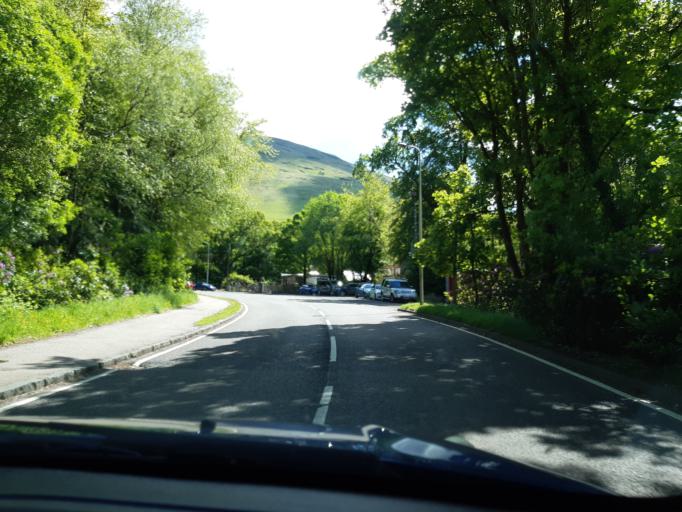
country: GB
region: Scotland
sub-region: Argyll and Bute
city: Garelochhead
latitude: 56.1985
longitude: -4.7450
